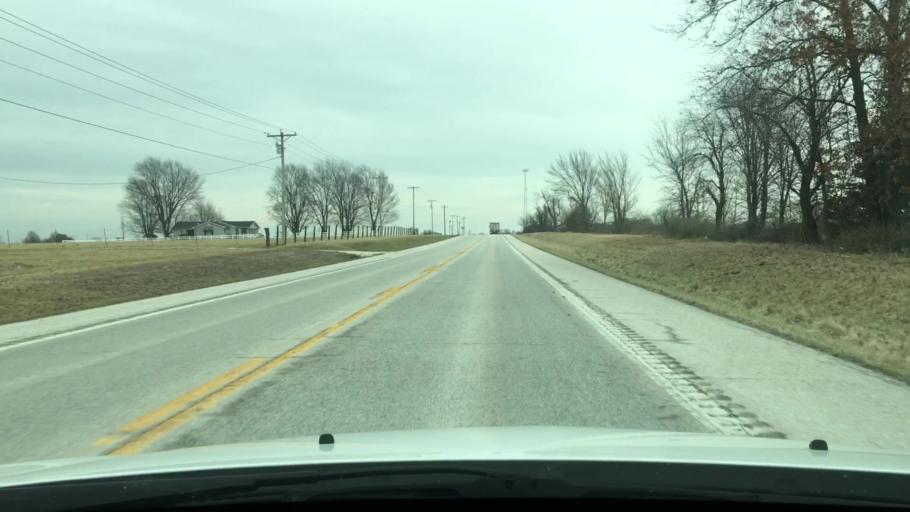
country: US
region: Missouri
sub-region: Pike County
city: Bowling Green
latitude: 39.3443
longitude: -91.2425
